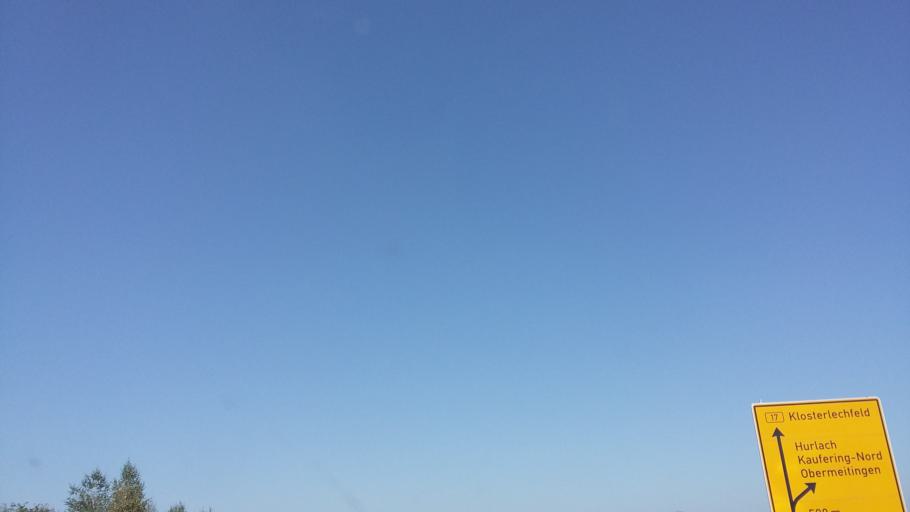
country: DE
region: Bavaria
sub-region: Upper Bavaria
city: Hurlach
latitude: 48.1198
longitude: 10.8340
